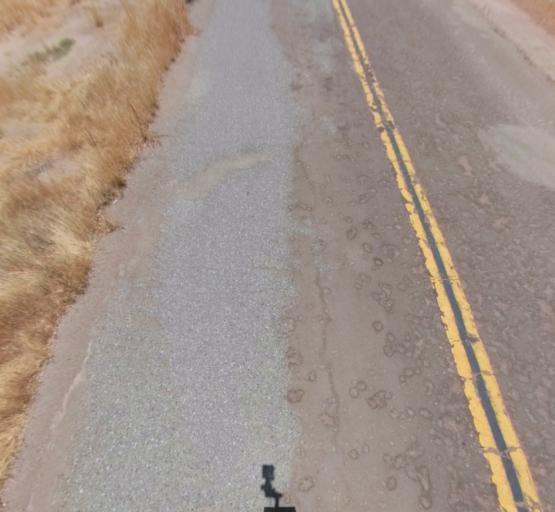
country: US
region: California
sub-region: Madera County
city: Fairmead
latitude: 37.0539
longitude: -120.1841
